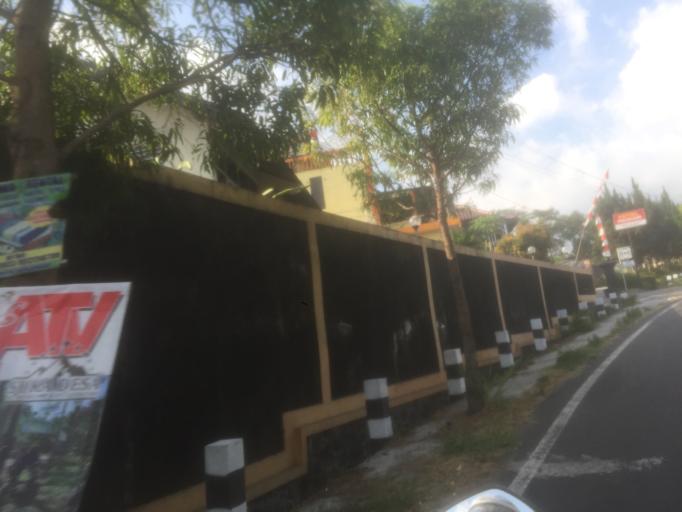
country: ID
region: Daerah Istimewa Yogyakarta
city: Sleman
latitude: -7.6569
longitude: 110.4226
